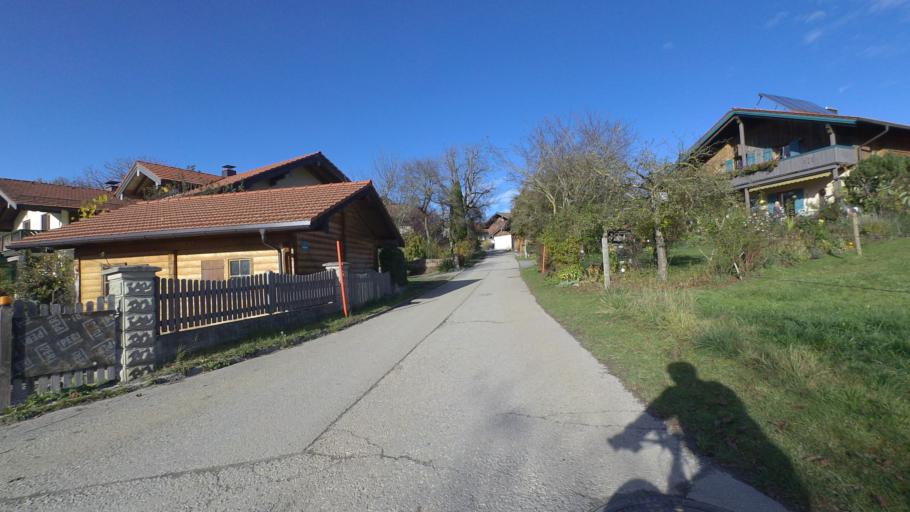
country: DE
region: Bavaria
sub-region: Upper Bavaria
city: Nussdorf
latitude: 47.9187
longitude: 12.5666
